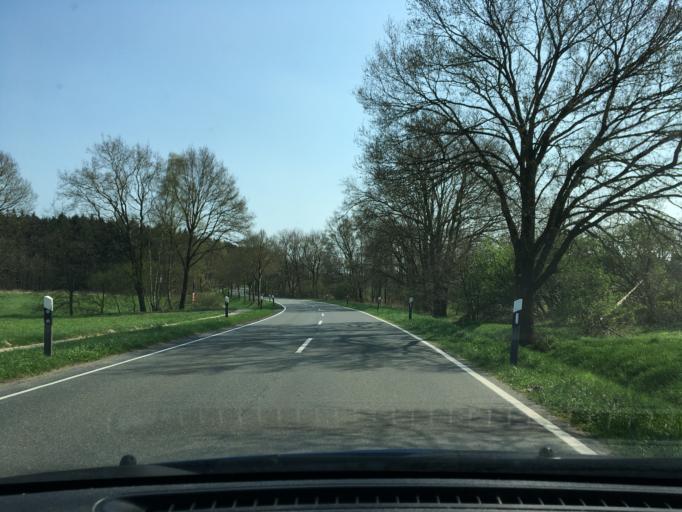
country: DE
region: Lower Saxony
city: Sudergellersen
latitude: 53.1985
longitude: 10.3046
